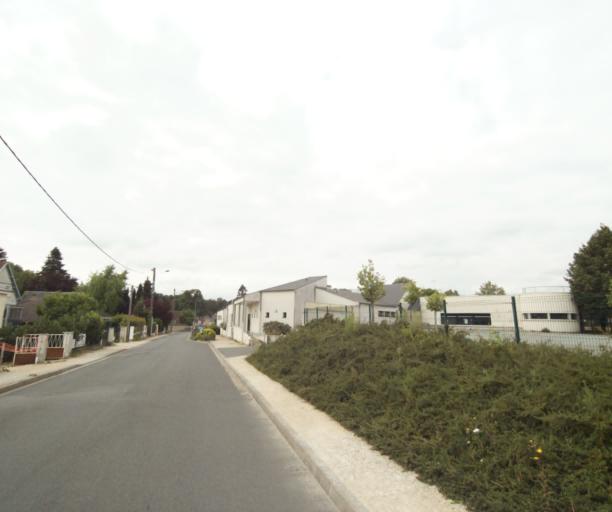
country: FR
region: Centre
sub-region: Departement du Loiret
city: Boigny-sur-Bionne
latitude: 47.9234
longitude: 2.0105
